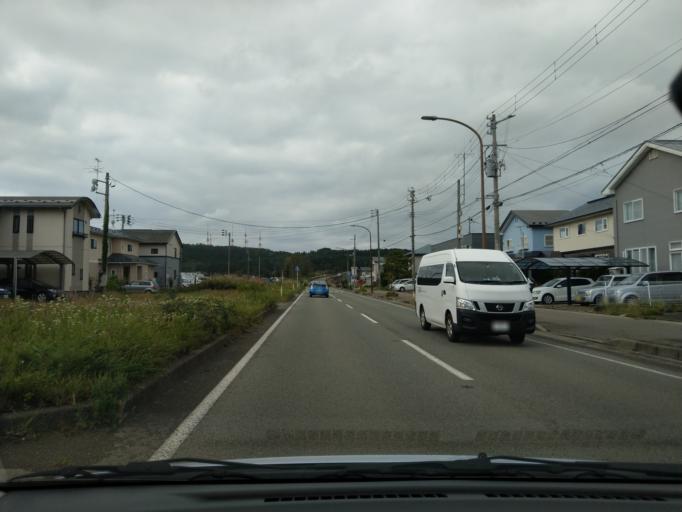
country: JP
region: Akita
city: Akita Shi
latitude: 39.6691
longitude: 140.0927
